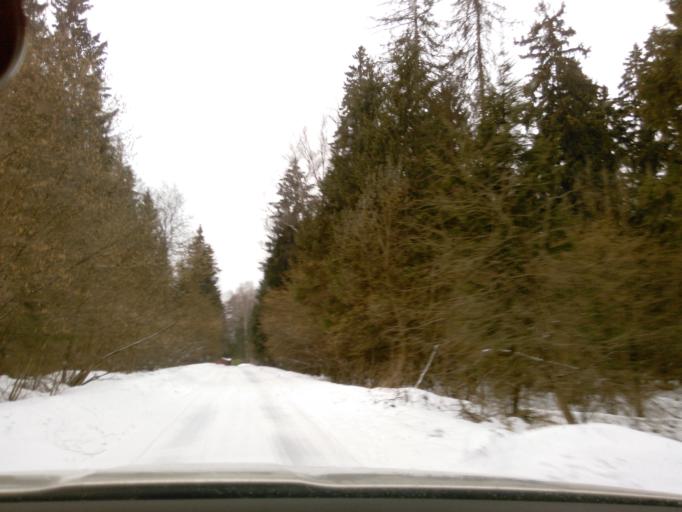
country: RU
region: Moskovskaya
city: Skhodnya
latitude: 55.9702
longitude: 37.2841
